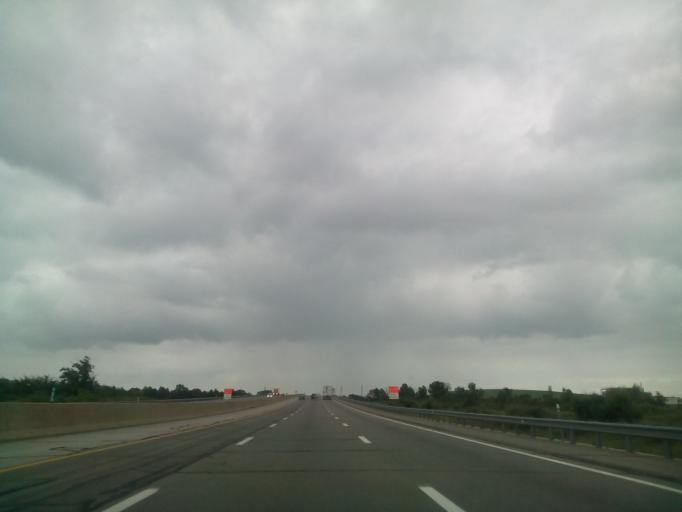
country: US
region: Ohio
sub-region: Sandusky County
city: Clyde
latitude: 41.3756
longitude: -82.9867
